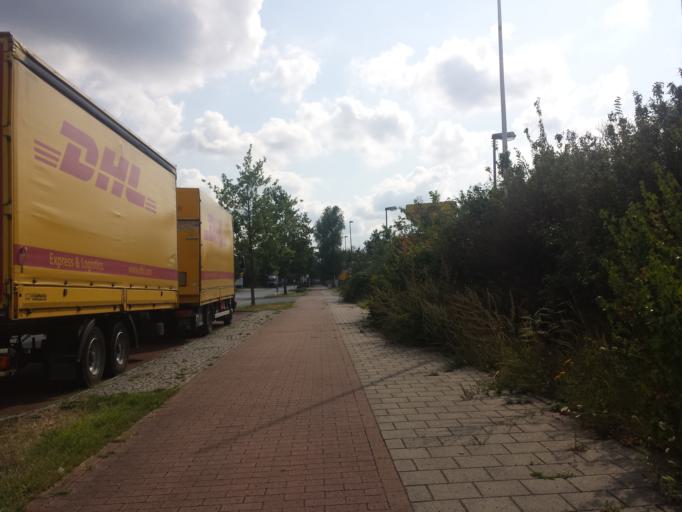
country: DE
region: Lower Saxony
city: Stuhr
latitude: 53.0959
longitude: 8.7014
